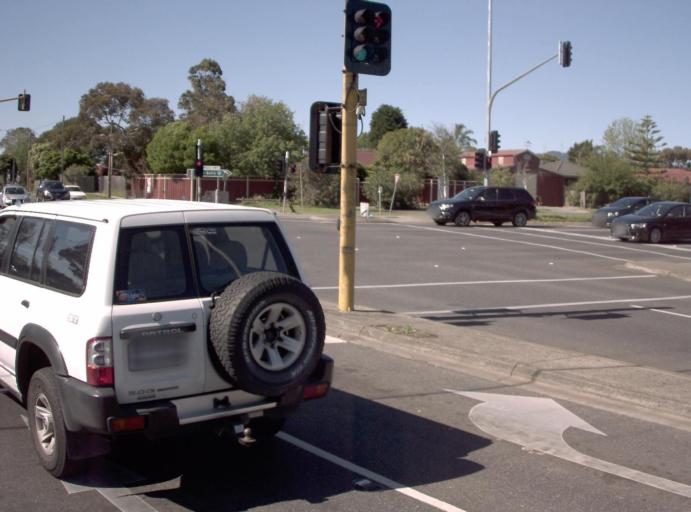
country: AU
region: Victoria
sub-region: Knox
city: Knoxfield
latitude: -37.8765
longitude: 145.2576
